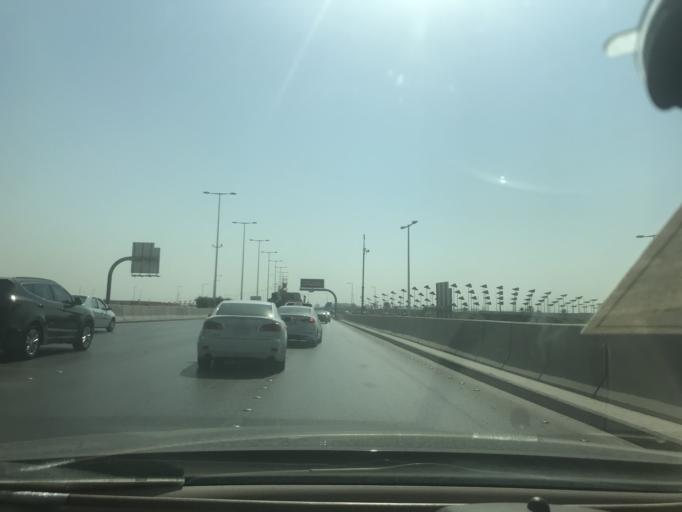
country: SA
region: Ar Riyad
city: Riyadh
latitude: 24.7276
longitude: 46.7095
